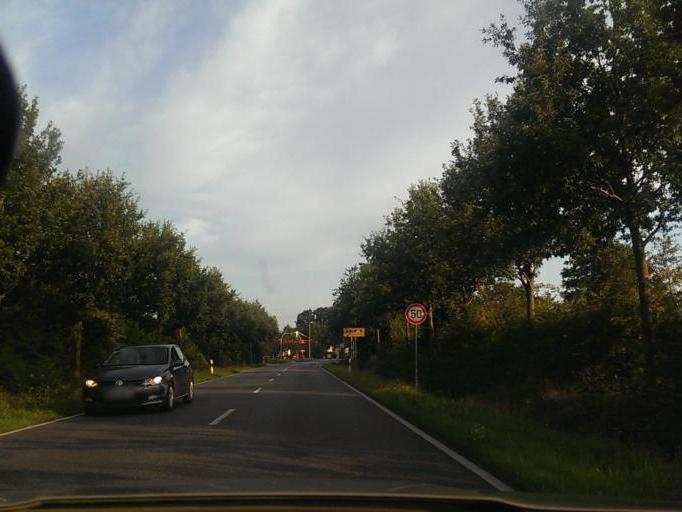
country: DE
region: Lower Saxony
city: Lilienthal
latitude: 53.1473
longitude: 8.9013
